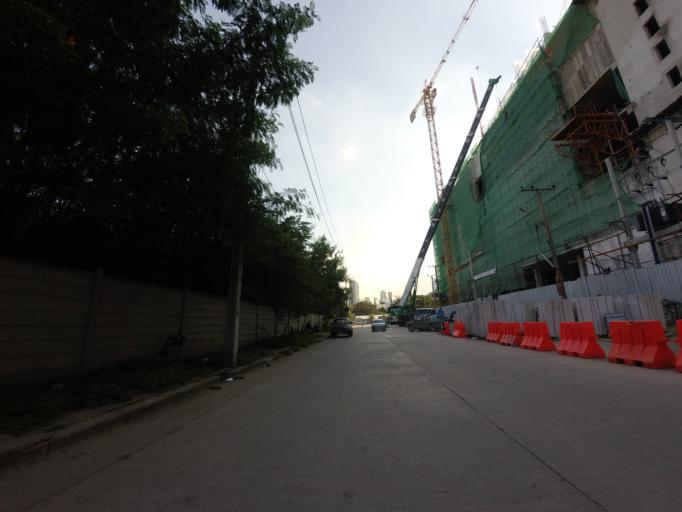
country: TH
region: Bangkok
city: Watthana
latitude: 13.7513
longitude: 100.5730
